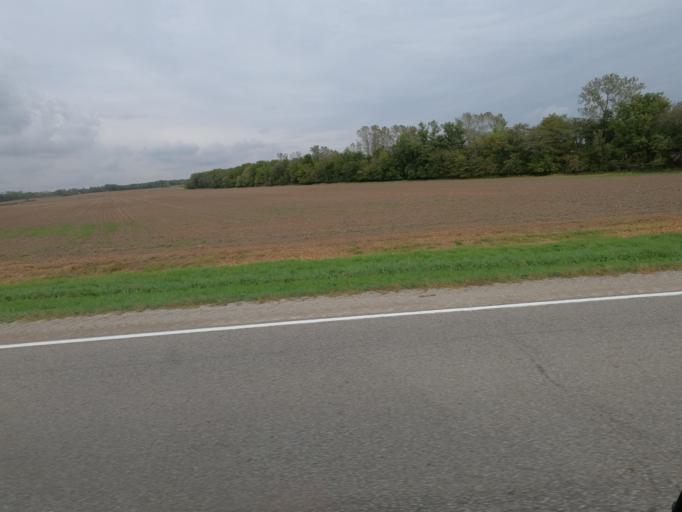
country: US
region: Iowa
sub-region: Jefferson County
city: Fairfield
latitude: 40.8936
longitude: -92.1804
